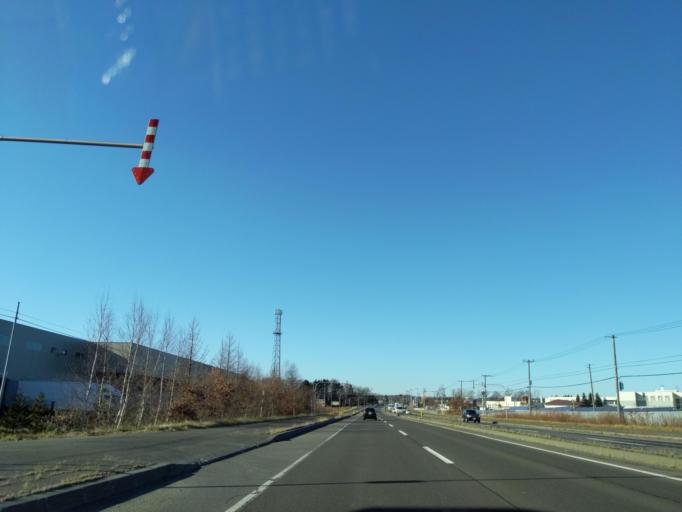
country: JP
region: Hokkaido
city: Kitahiroshima
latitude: 42.9370
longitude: 141.5120
